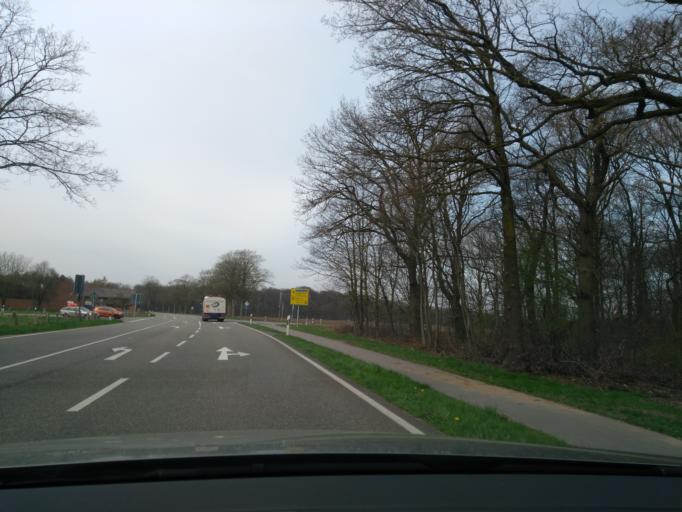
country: DE
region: North Rhine-Westphalia
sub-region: Regierungsbezirk Dusseldorf
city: Issum
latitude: 51.5840
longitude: 6.4330
